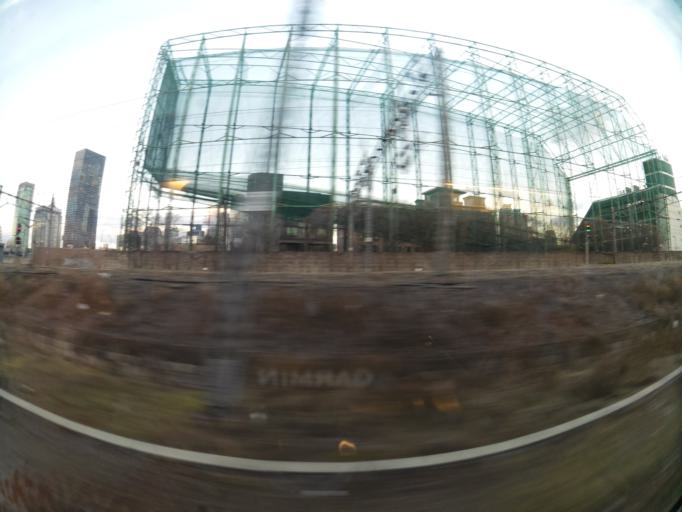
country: KR
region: Gyeonggi-do
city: Kwangmyong
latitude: 37.5160
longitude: 126.9202
